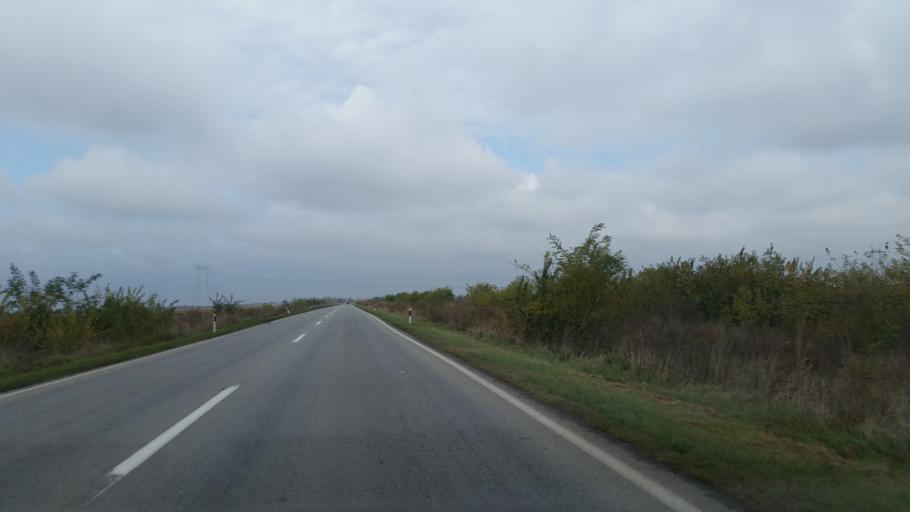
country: RS
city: Melenci
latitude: 45.4881
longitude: 20.3314
